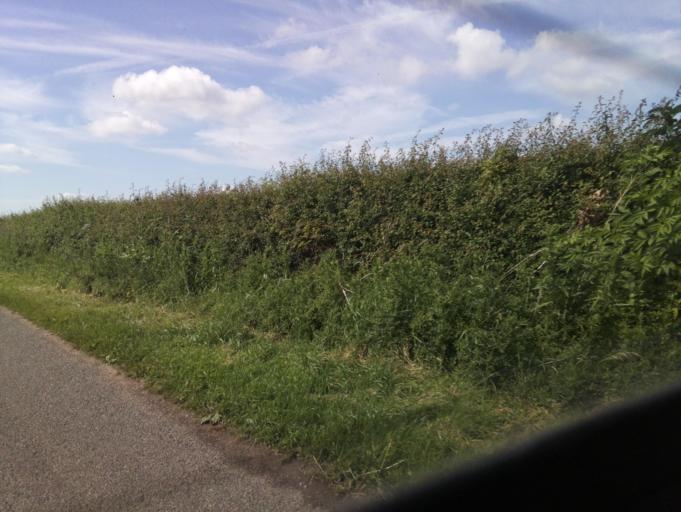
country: GB
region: England
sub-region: Lincolnshire
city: Skellingthorpe
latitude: 53.1435
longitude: -0.6331
